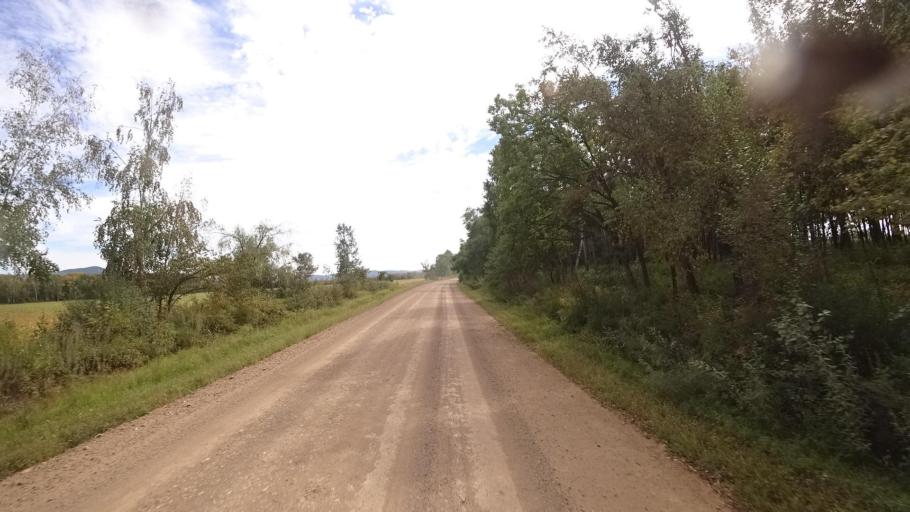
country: RU
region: Primorskiy
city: Yakovlevka
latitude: 44.5207
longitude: 133.5958
